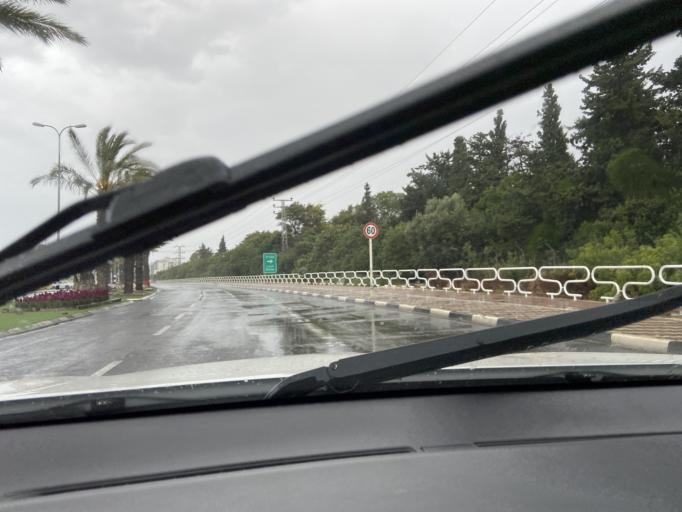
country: IL
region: Northern District
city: El Mazra`a
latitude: 32.9910
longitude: 35.0964
